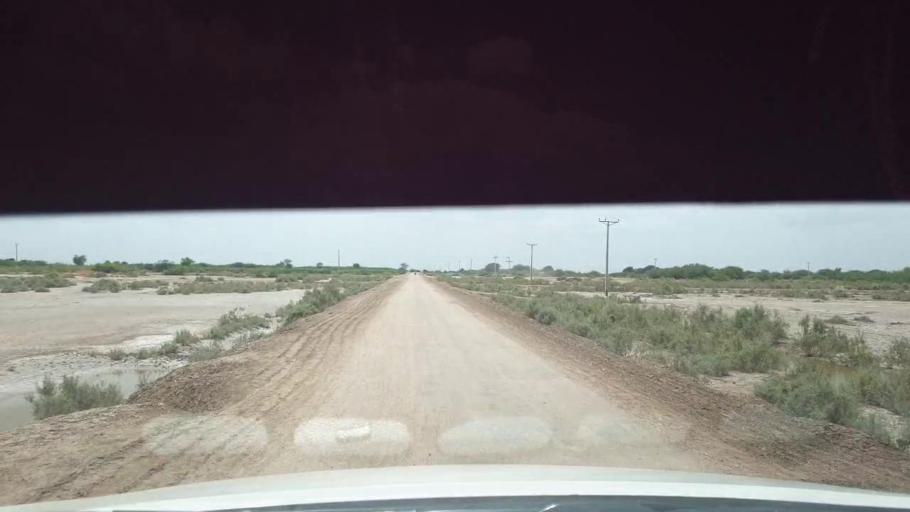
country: PK
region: Sindh
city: Kadhan
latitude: 24.5462
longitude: 69.1145
